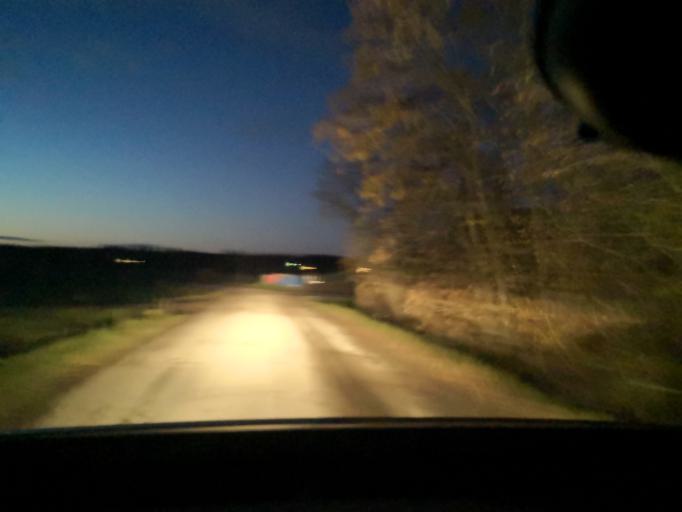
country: SE
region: Uppsala
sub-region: Heby Kommun
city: Heby
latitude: 59.9342
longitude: 16.7524
